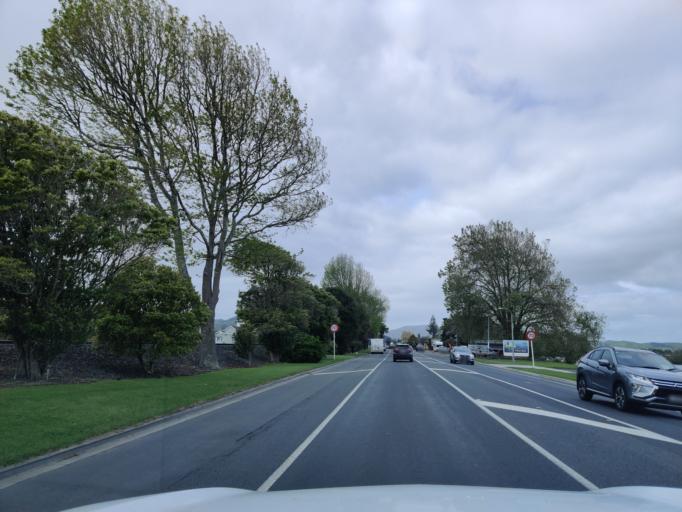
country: NZ
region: Waikato
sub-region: Waikato District
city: Ngaruawahia
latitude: -37.5480
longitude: 175.1585
